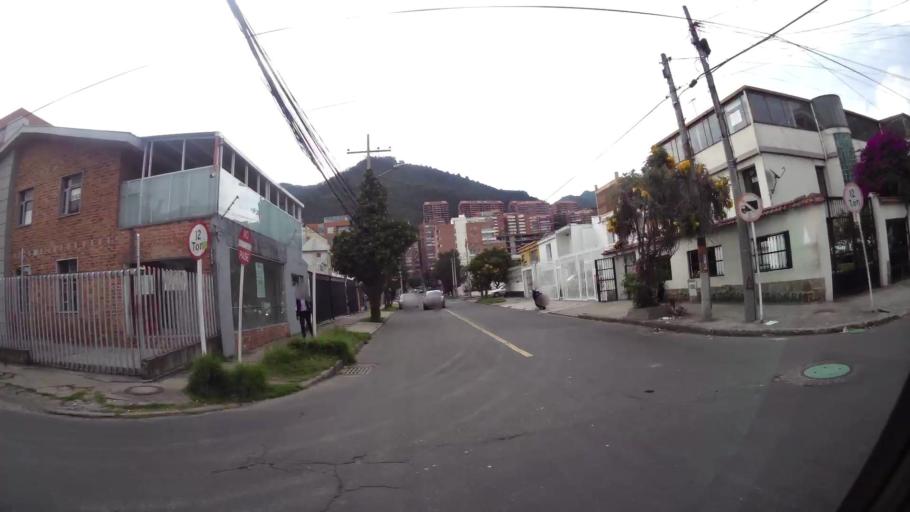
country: CO
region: Bogota D.C.
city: Barrio San Luis
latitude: 4.7017
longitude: -74.0317
